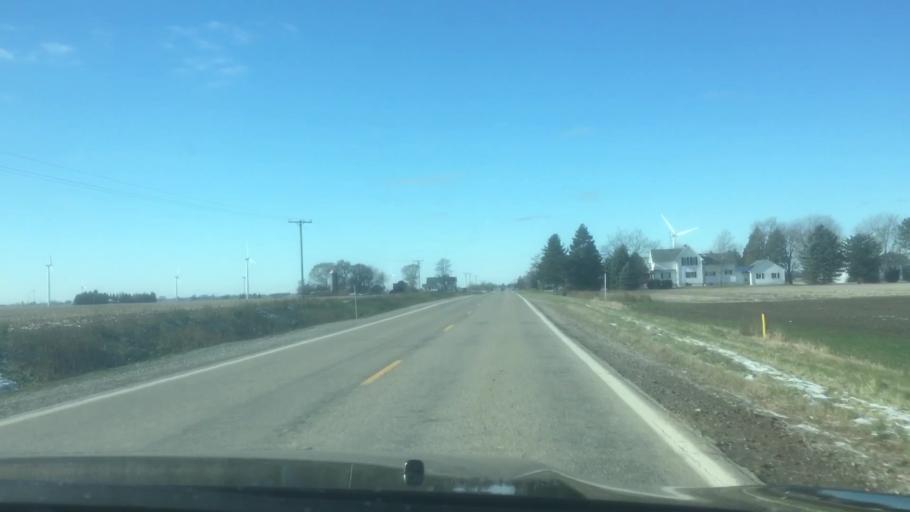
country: US
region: Michigan
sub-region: Tuscola County
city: Reese
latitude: 43.5229
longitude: -83.6316
